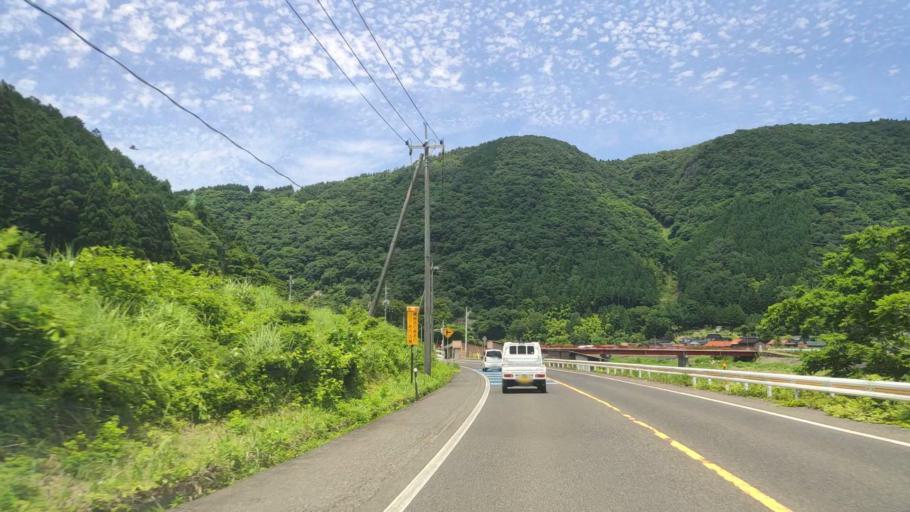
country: JP
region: Tottori
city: Tottori
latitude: 35.3662
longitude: 134.3777
